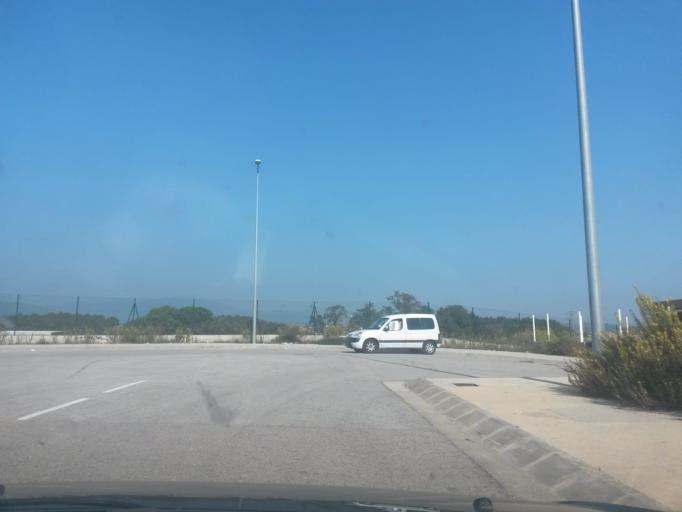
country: ES
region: Catalonia
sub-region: Provincia de Girona
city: Fornells de la Selva
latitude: 41.9442
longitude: 2.8008
